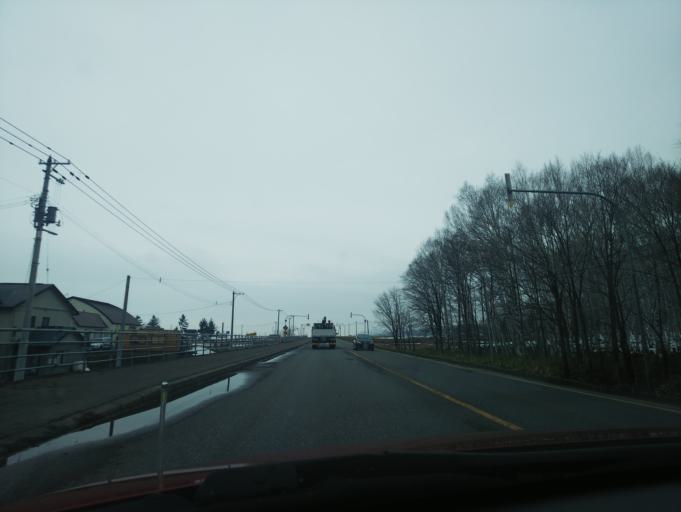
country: JP
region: Hokkaido
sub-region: Asahikawa-shi
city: Asahikawa
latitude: 44.0602
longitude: 142.4032
